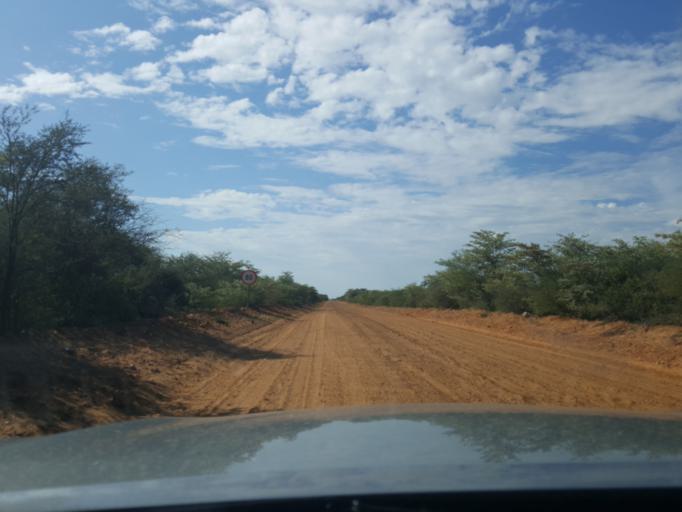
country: BW
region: Kweneng
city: Khudumelapye
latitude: -23.6316
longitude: 24.7287
